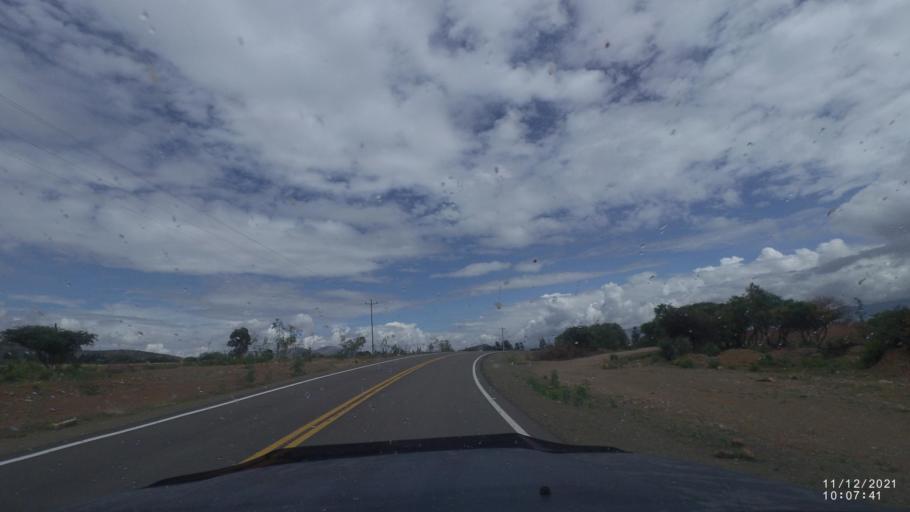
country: BO
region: Cochabamba
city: Tarata
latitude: -17.6776
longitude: -65.9585
